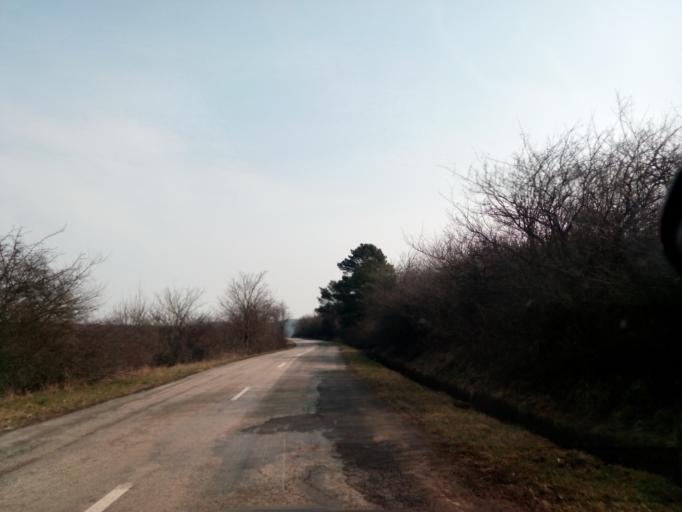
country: HU
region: Borsod-Abauj-Zemplen
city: Satoraljaujhely
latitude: 48.4698
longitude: 21.6582
